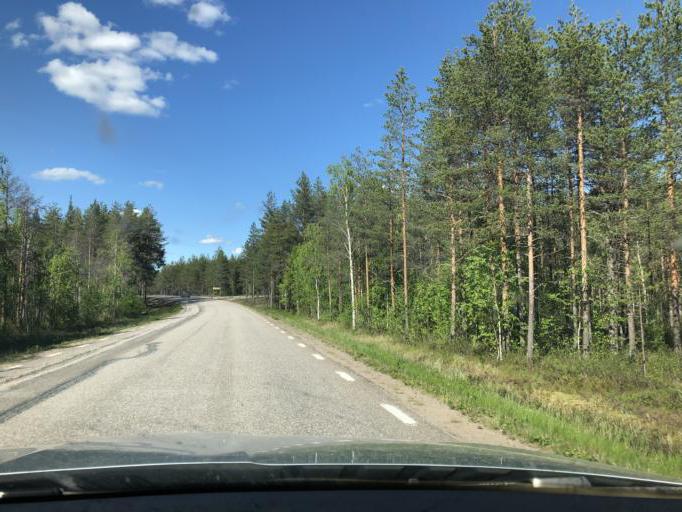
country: SE
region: Norrbotten
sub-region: Kalix Kommun
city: Kalix
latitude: 65.9043
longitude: 23.1732
